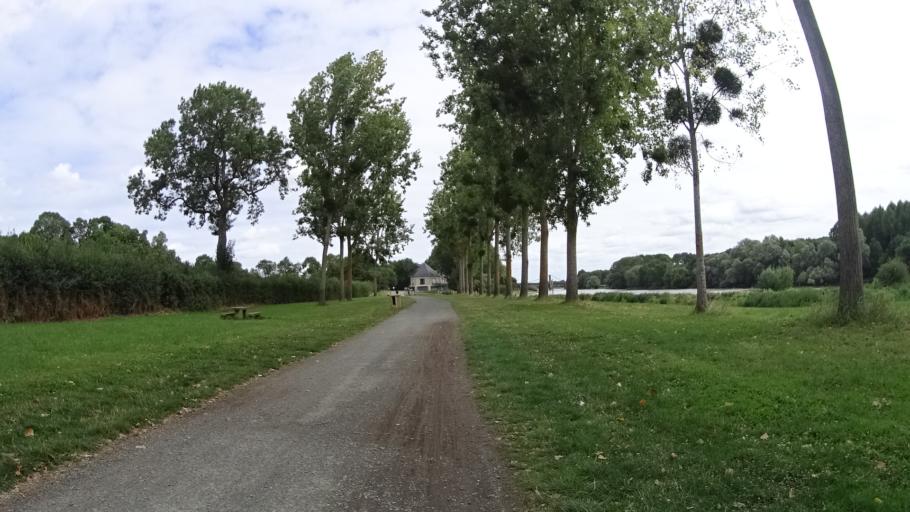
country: FR
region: Pays de la Loire
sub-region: Departement de Maine-et-Loire
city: Bouchemaine
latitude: 47.4138
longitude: -0.6155
